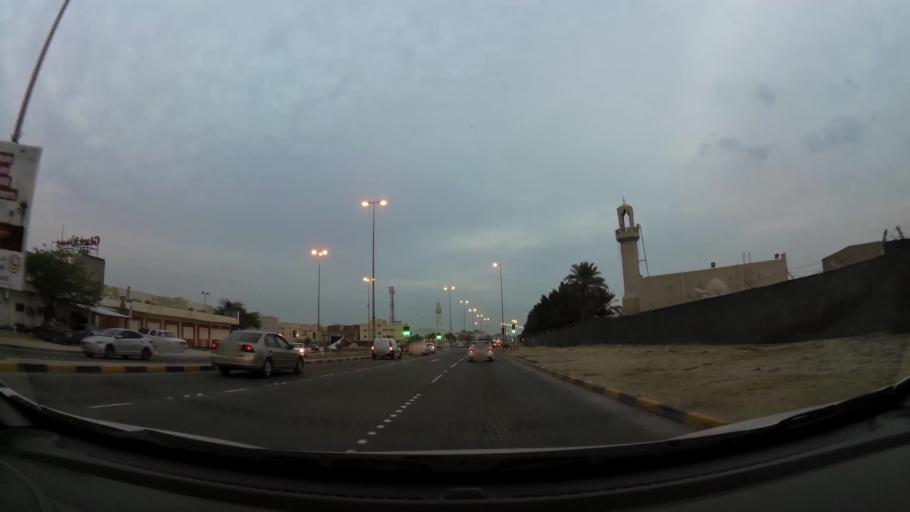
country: BH
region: Northern
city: Ar Rifa'
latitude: 26.1132
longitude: 50.5772
